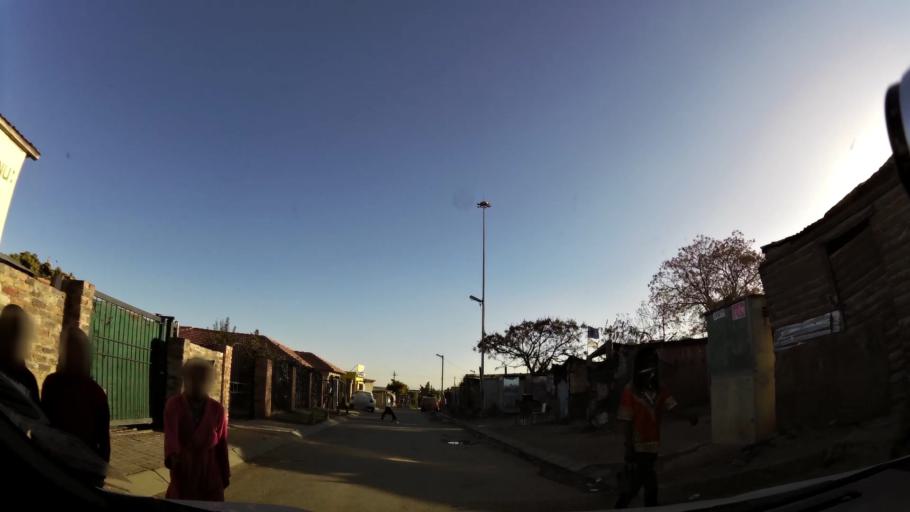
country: ZA
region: Gauteng
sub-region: City of Johannesburg Metropolitan Municipality
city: Diepsloot
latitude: -25.9175
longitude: 28.0217
